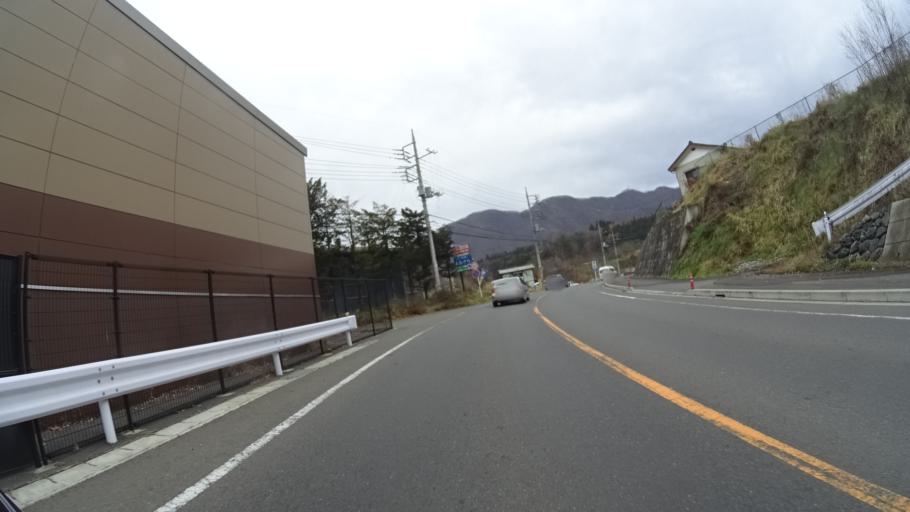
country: JP
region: Gunma
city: Numata
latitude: 36.6706
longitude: 139.1905
